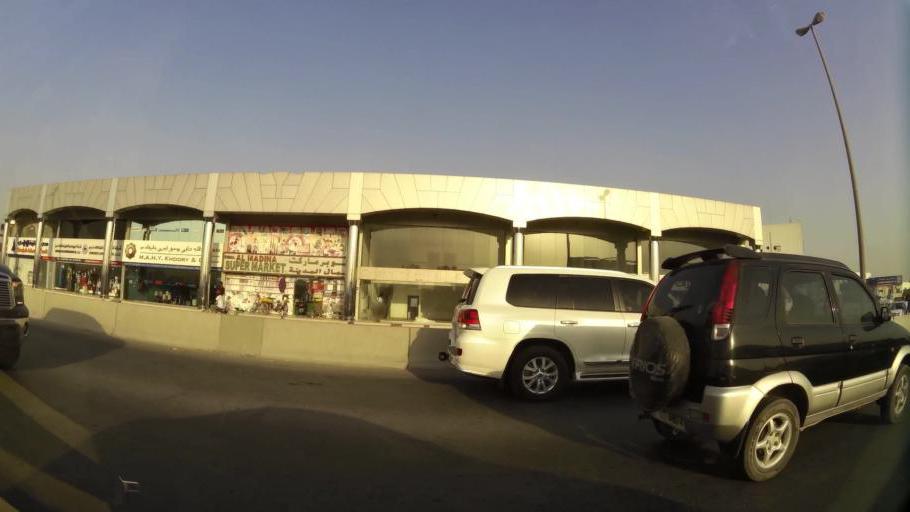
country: AE
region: Ash Shariqah
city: Sharjah
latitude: 25.3231
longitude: 55.4040
